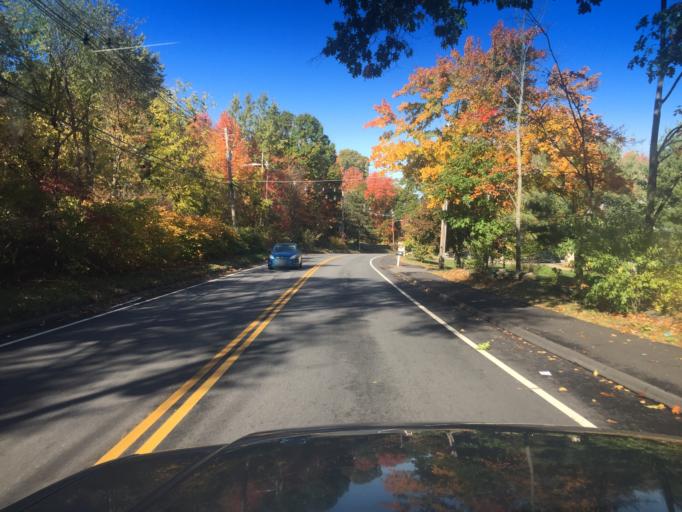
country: US
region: Massachusetts
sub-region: Middlesex County
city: Hudson
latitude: 42.3839
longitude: -71.5492
